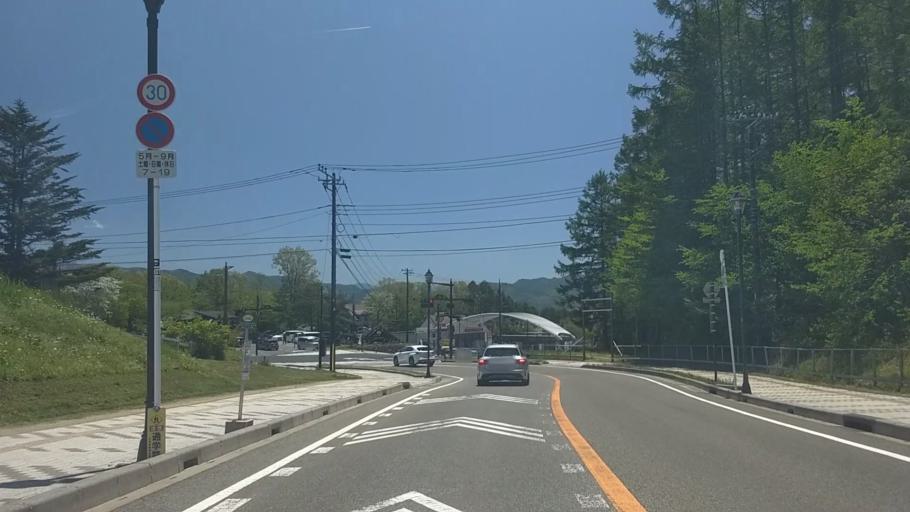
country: JP
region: Yamanashi
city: Nirasaki
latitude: 35.9161
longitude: 138.4408
